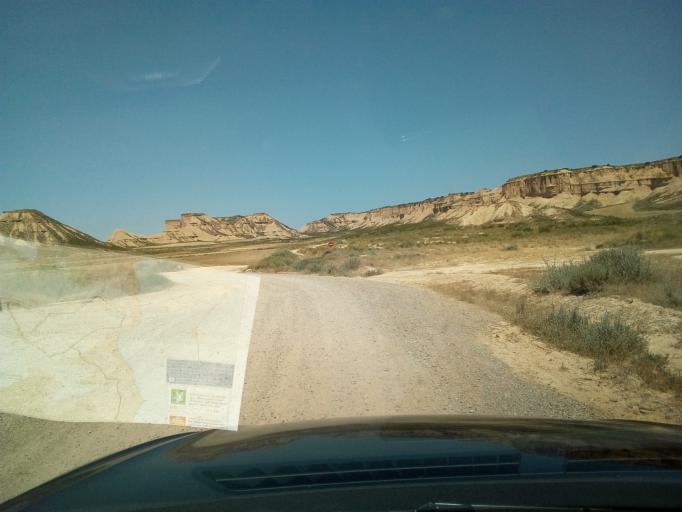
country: ES
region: Aragon
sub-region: Provincia de Zaragoza
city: Sadaba
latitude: 42.1937
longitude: -1.4131
